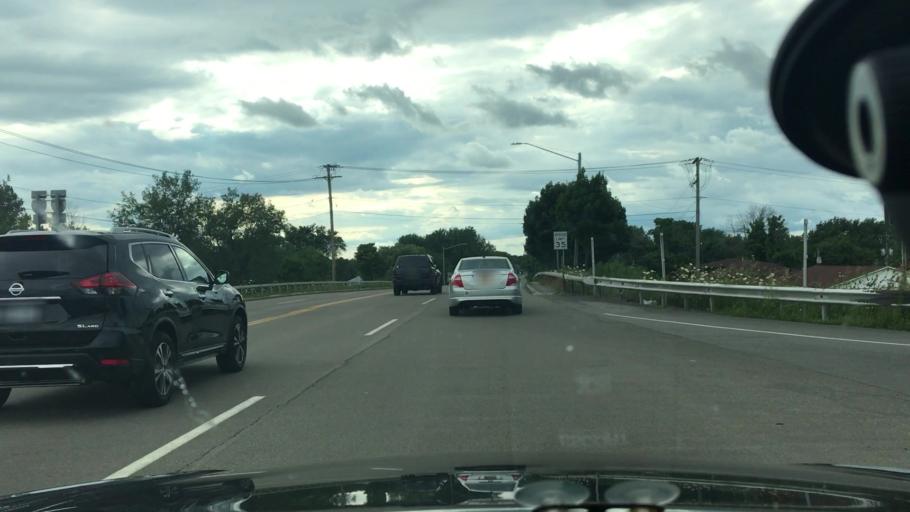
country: US
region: New York
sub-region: Erie County
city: West Seneca
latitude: 42.8282
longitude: -78.7933
